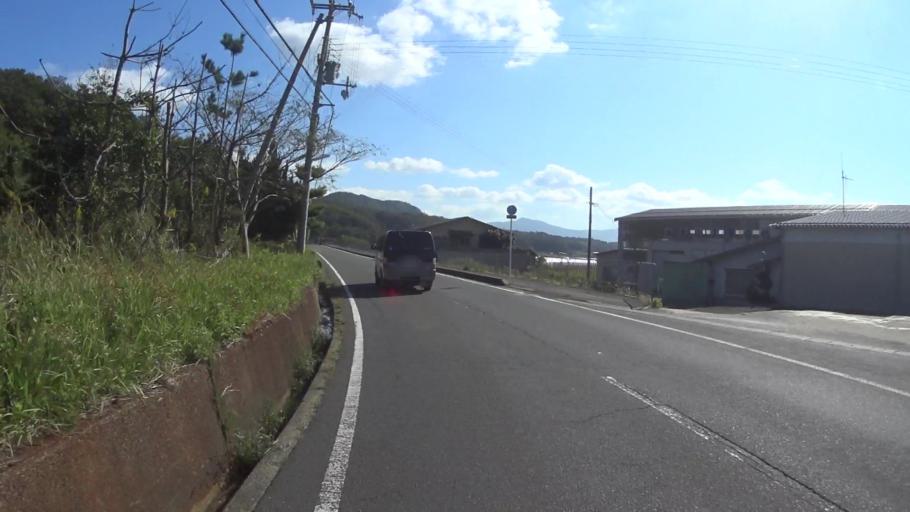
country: JP
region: Kyoto
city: Miyazu
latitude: 35.6935
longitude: 135.0430
